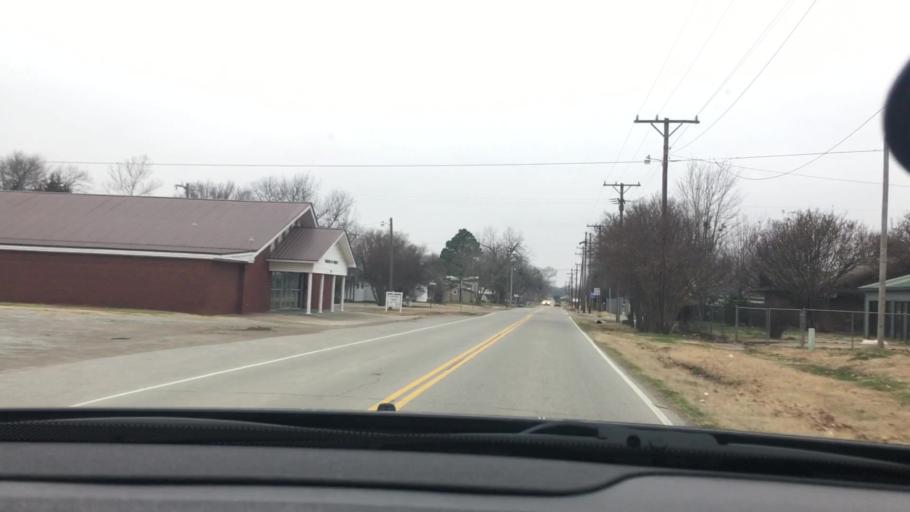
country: US
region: Oklahoma
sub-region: Coal County
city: Coalgate
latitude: 34.5400
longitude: -96.2213
